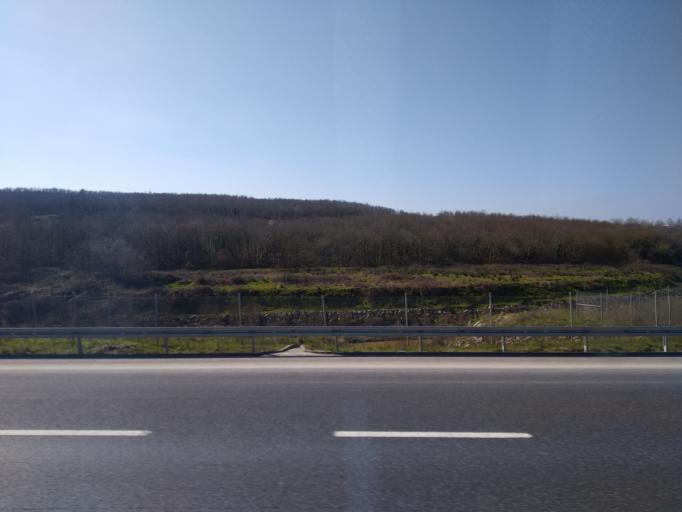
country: TR
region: Istanbul
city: Mahmut Sevket Pasa
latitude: 41.1111
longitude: 29.2921
